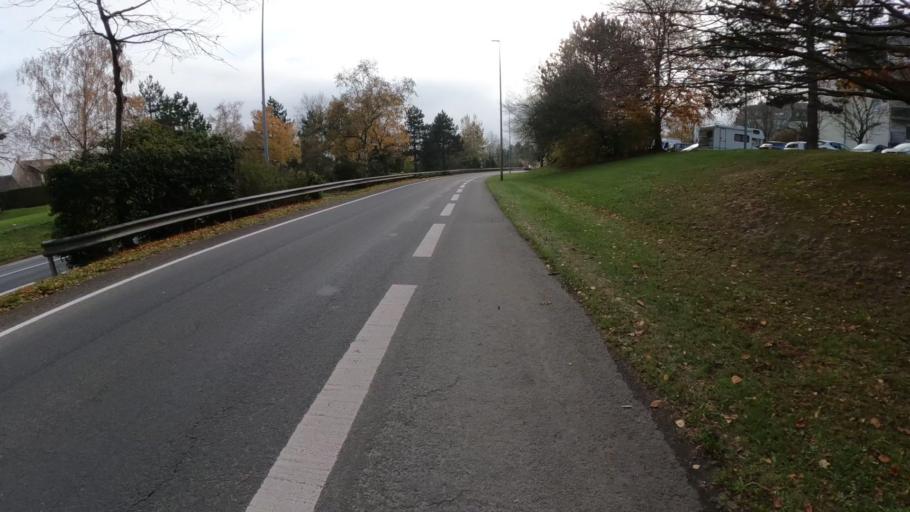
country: FR
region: Lower Normandy
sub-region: Departement du Calvados
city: Epron
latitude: 49.2036
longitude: -0.3752
